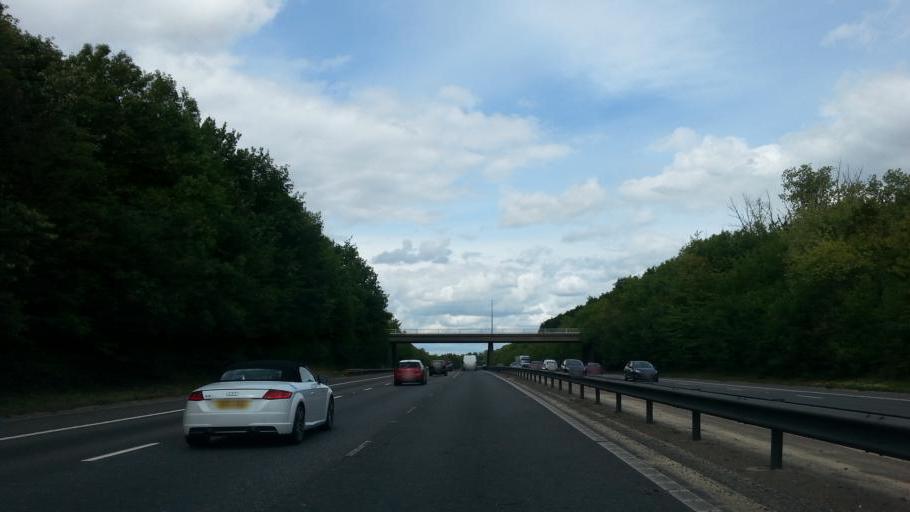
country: GB
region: England
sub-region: Hertfordshire
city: Sawbridgeworth
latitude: 51.8011
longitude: 0.1757
